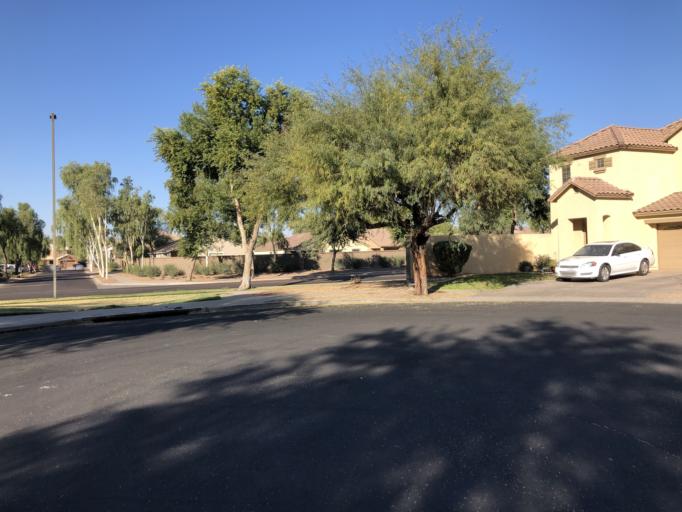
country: US
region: Arizona
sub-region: Maricopa County
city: Queen Creek
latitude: 33.2709
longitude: -111.7068
